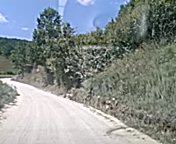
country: BA
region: Federation of Bosnia and Herzegovina
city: Orasac
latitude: 44.6212
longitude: 16.0613
